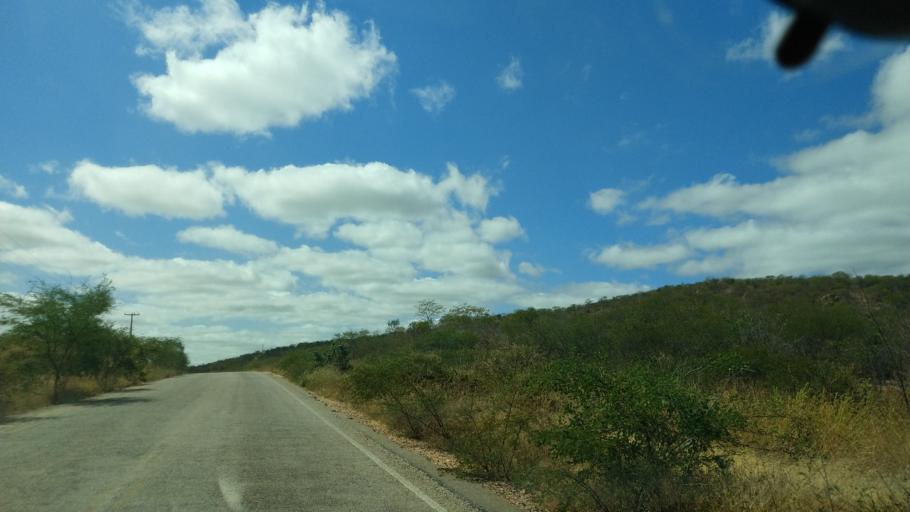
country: BR
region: Rio Grande do Norte
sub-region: Currais Novos
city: Currais Novos
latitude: -6.2619
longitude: -36.5821
